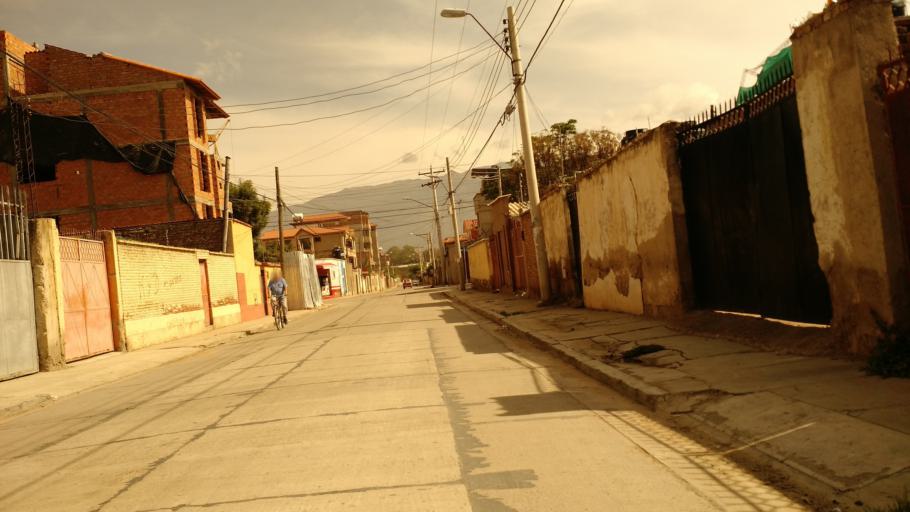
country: BO
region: Cochabamba
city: Cochabamba
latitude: -17.4251
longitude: -66.1597
